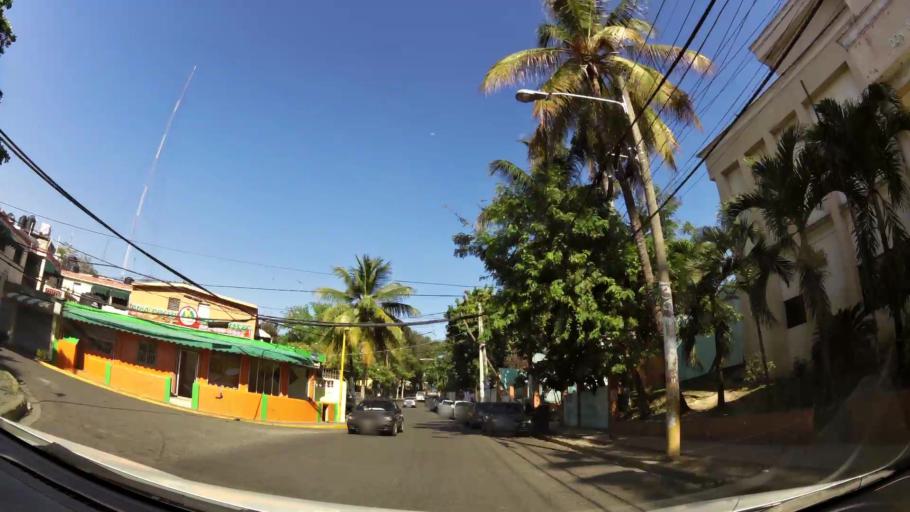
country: DO
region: Nacional
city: Santo Domingo
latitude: 18.4734
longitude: -69.9936
